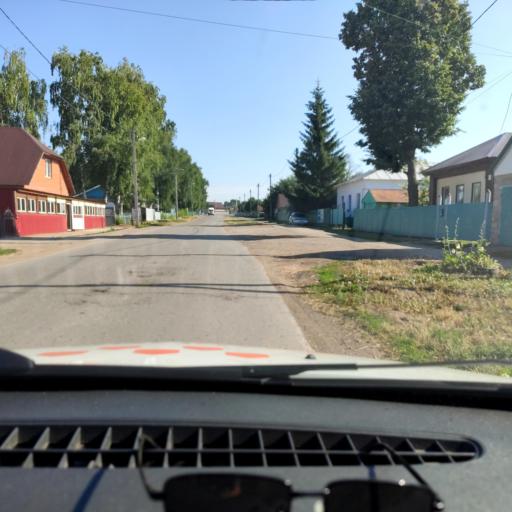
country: RU
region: Bashkortostan
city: Tolbazy
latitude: 54.0130
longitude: 55.8839
